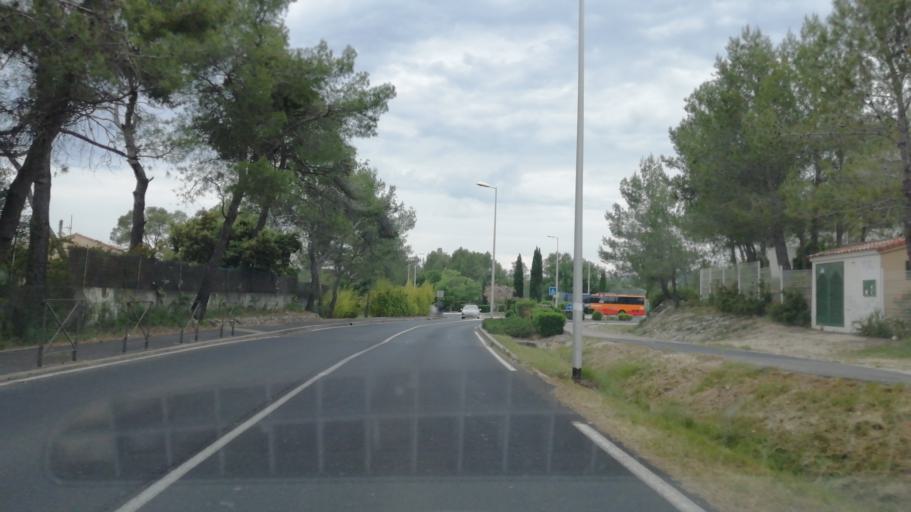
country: FR
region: Languedoc-Roussillon
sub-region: Departement de l'Herault
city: Saint-Clement-de-Riviere
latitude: 43.7064
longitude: 3.8312
